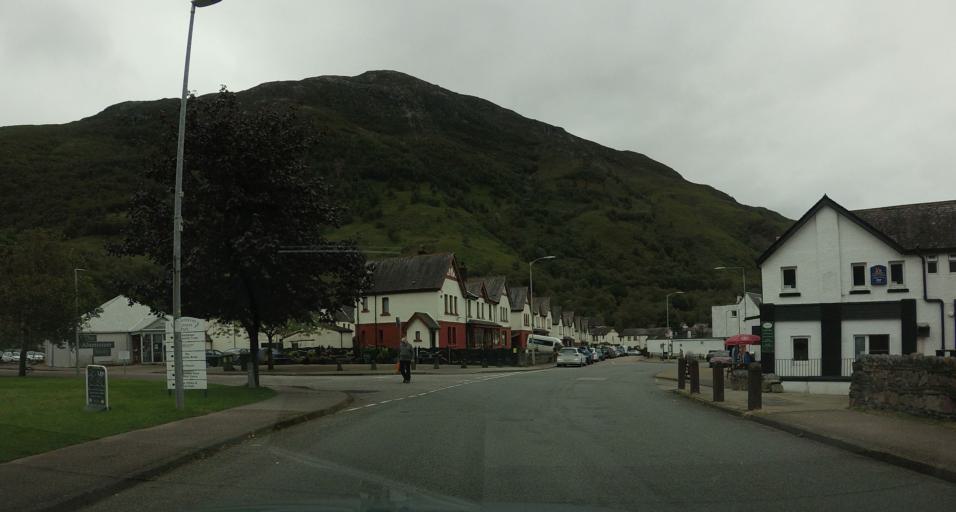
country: GB
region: Scotland
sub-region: Highland
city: Fort William
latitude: 56.7135
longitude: -4.9629
